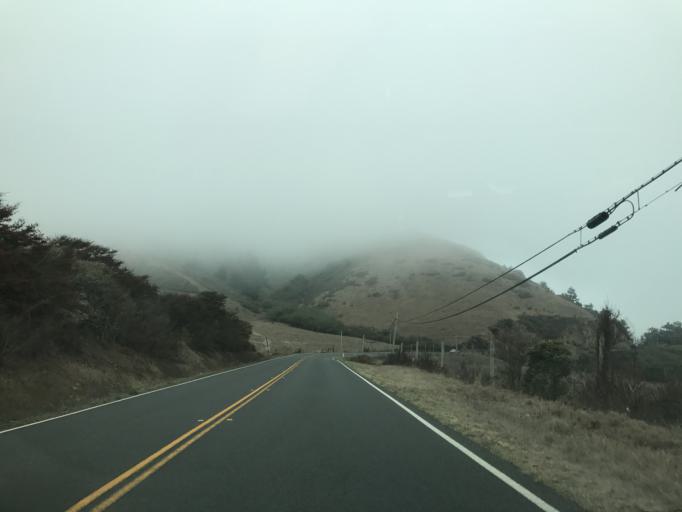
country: US
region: California
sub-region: Sonoma County
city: Monte Rio
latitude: 38.4413
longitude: -123.1006
